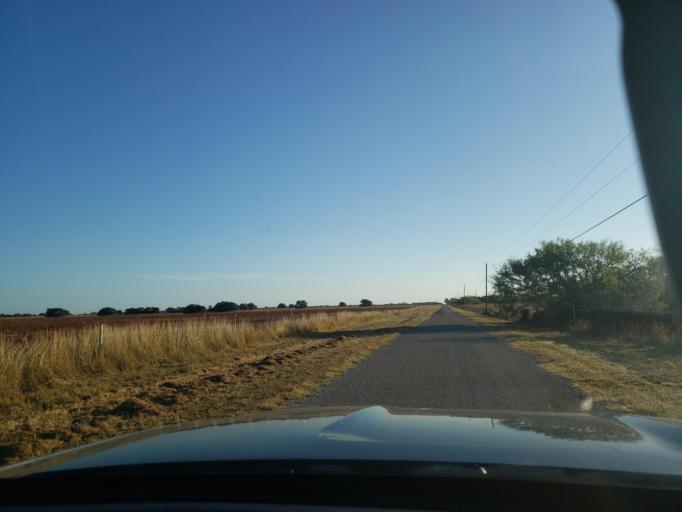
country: US
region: Texas
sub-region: Bee County
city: Beeville
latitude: 28.4268
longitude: -97.6986
